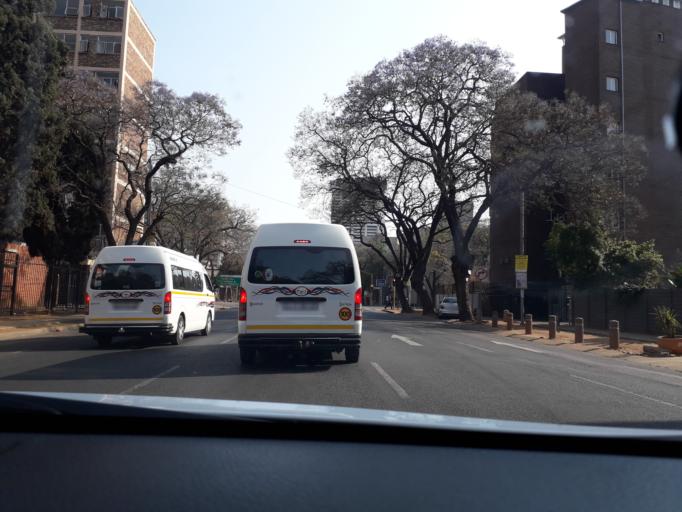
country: ZA
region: Gauteng
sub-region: City of Tshwane Metropolitan Municipality
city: Pretoria
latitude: -25.7526
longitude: 28.1935
